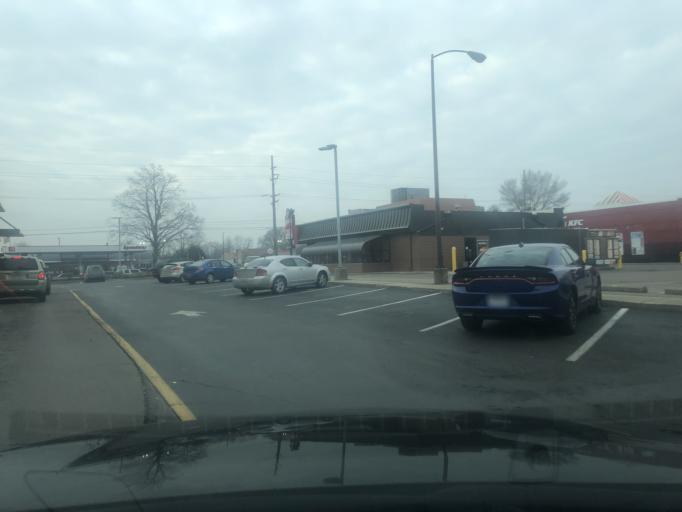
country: US
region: Michigan
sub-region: Wayne County
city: Belleville
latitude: 42.2140
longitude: -83.5425
